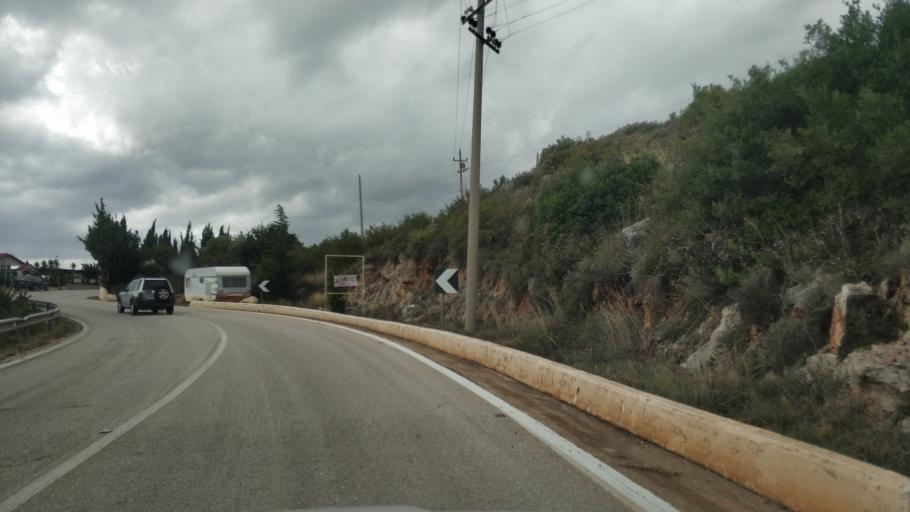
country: AL
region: Vlore
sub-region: Rrethi i Vlores
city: Vranisht
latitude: 40.1453
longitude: 19.6454
